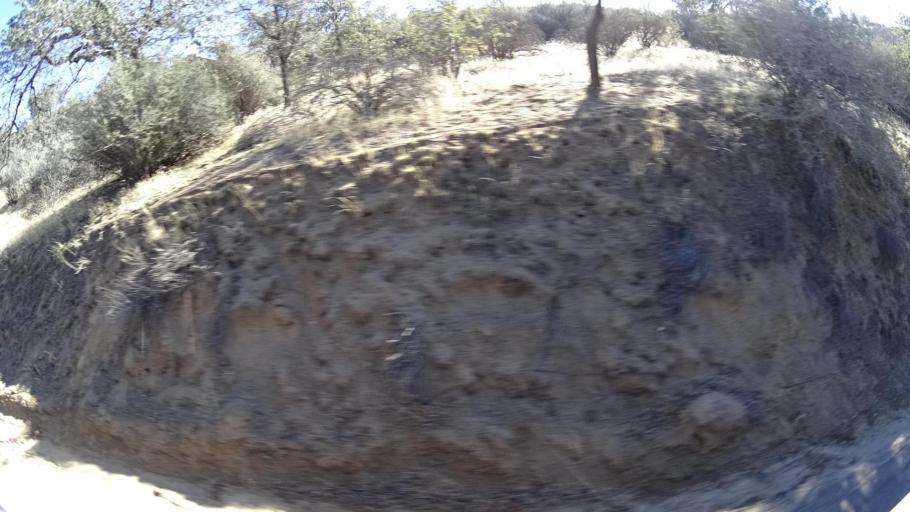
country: US
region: California
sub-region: Kern County
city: Bodfish
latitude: 35.5901
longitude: -118.5003
